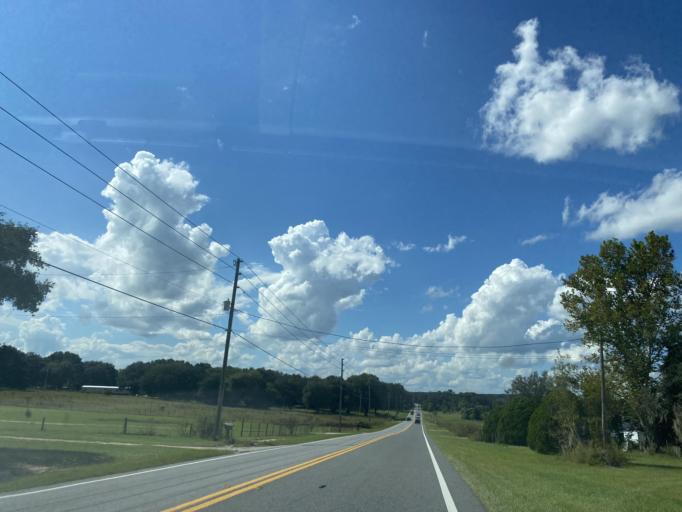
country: US
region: Florida
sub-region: Lake County
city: Lady Lake
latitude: 28.9811
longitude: -81.8812
